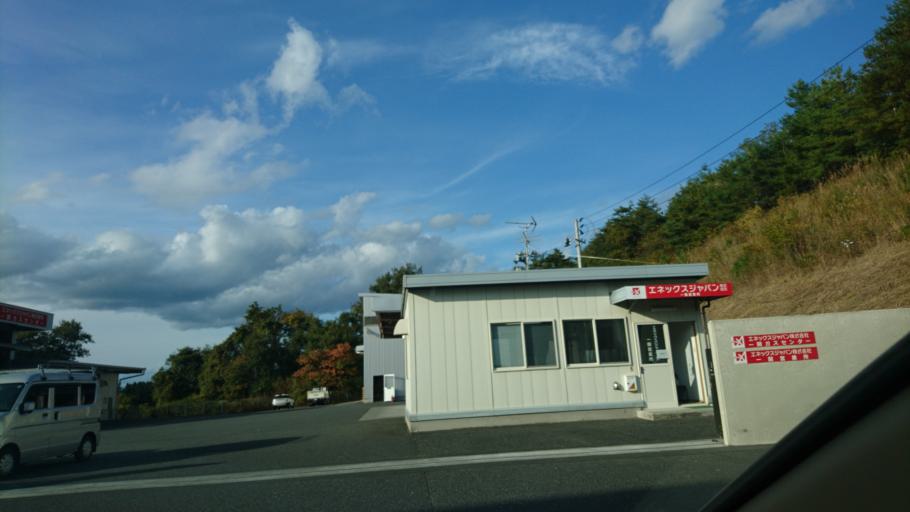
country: JP
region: Iwate
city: Ichinoseki
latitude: 38.8791
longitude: 141.1393
